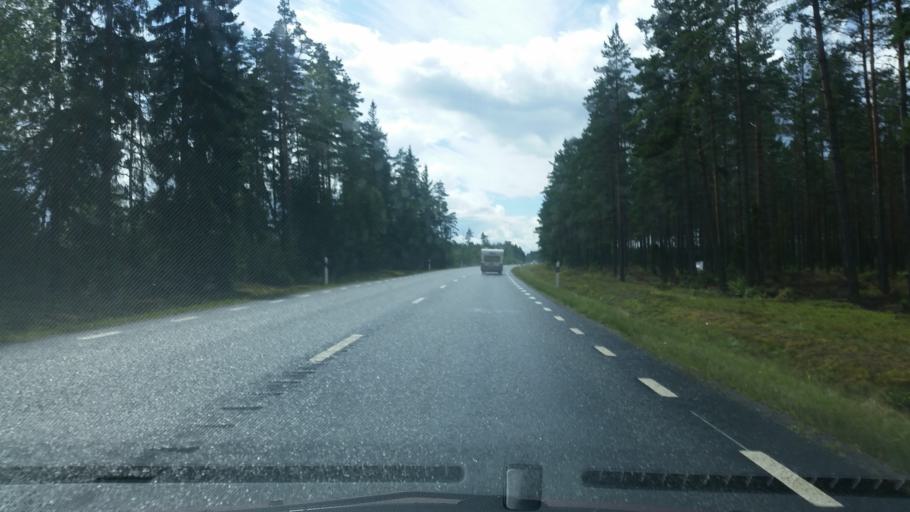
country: SE
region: Joenkoeping
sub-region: Gislaveds Kommun
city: Gislaved
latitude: 57.4036
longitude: 13.5979
